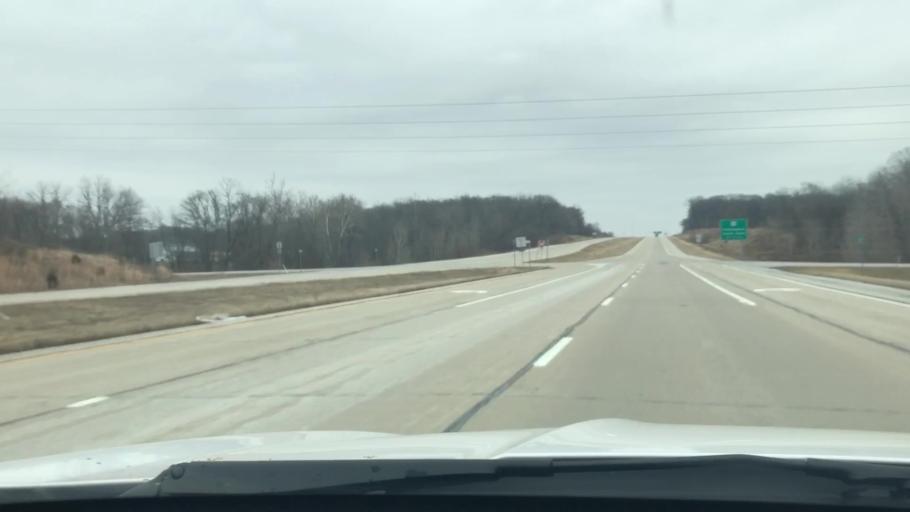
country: US
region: Indiana
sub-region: Miami County
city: Peru
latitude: 40.7702
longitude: -86.1500
